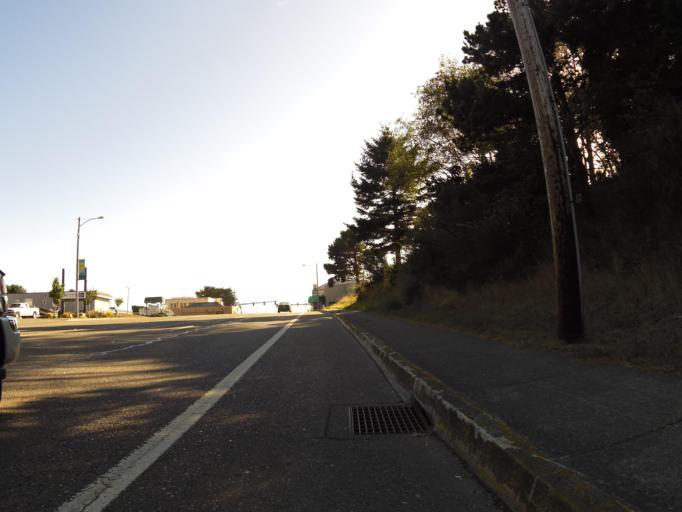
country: US
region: Oregon
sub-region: Curry County
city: Gold Beach
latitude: 42.4188
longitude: -124.4190
